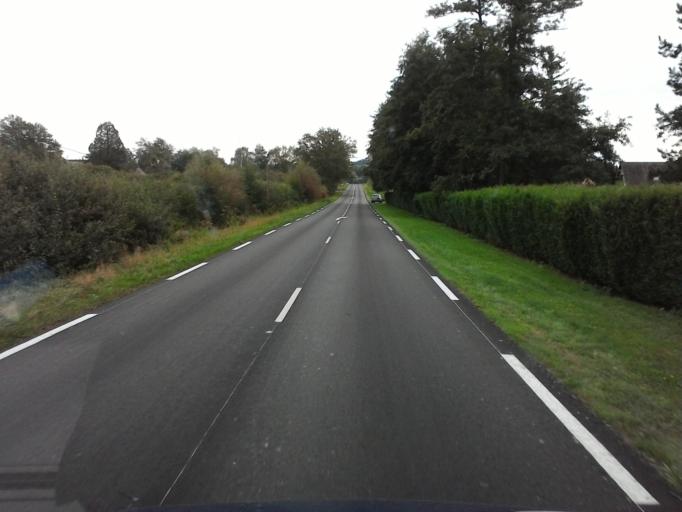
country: FR
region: Bourgogne
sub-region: Departement de Saone-et-Loire
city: Saint-Vallier
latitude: 46.6529
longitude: 4.4175
